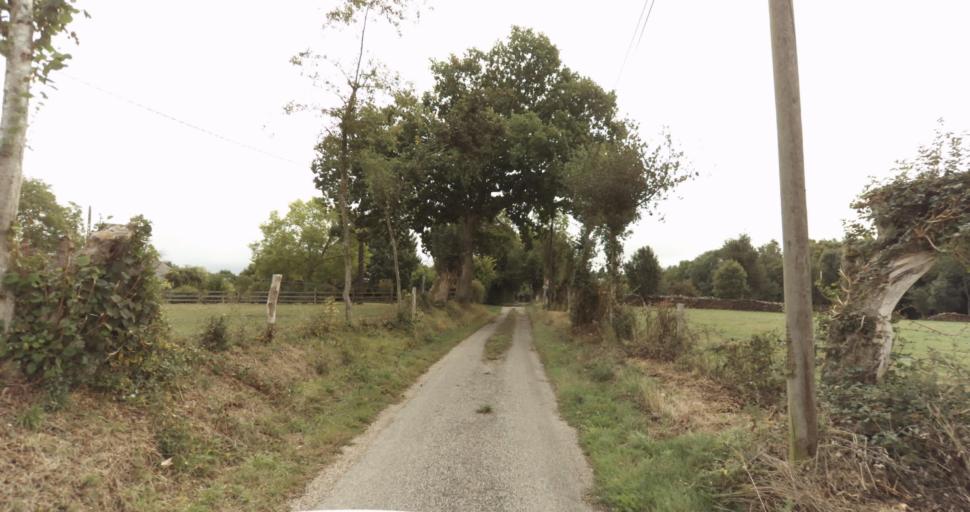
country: FR
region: Lower Normandy
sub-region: Departement de l'Orne
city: Vimoutiers
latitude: 48.9298
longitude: 0.1838
